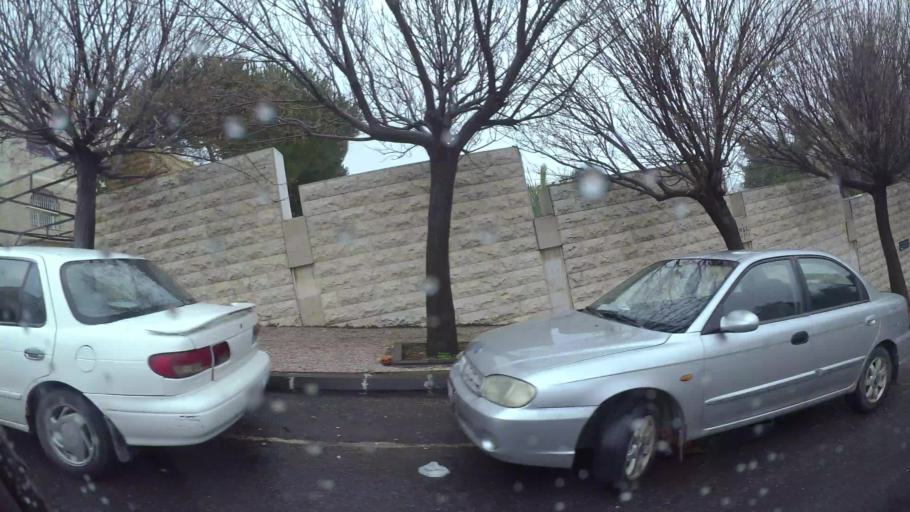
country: JO
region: Amman
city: Wadi as Sir
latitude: 31.9981
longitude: 35.8173
